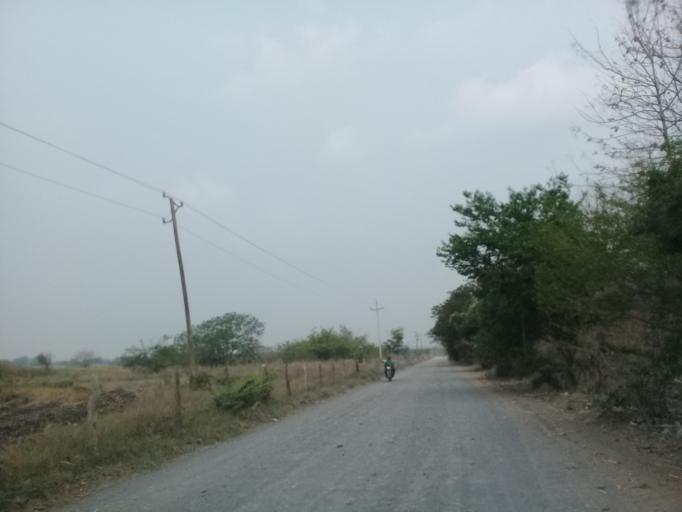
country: MX
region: Veracruz
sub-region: Medellin
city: La Laguna y Monte del Castillo
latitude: 18.9027
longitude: -96.1757
